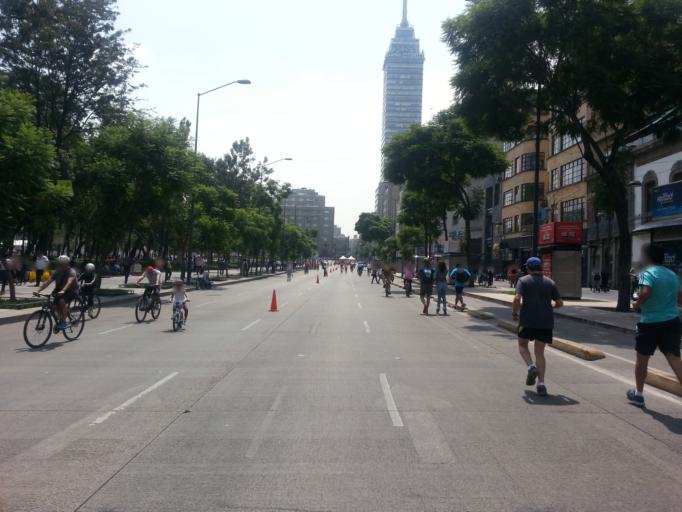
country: MX
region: Mexico City
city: Cuauhtemoc
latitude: 19.4346
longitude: -99.1437
